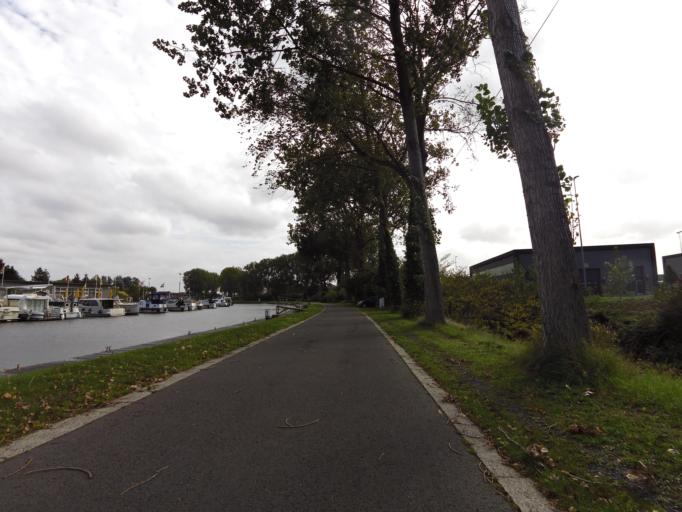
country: BE
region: Flanders
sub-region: Provincie West-Vlaanderen
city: Brugge
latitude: 51.1950
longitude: 3.2251
